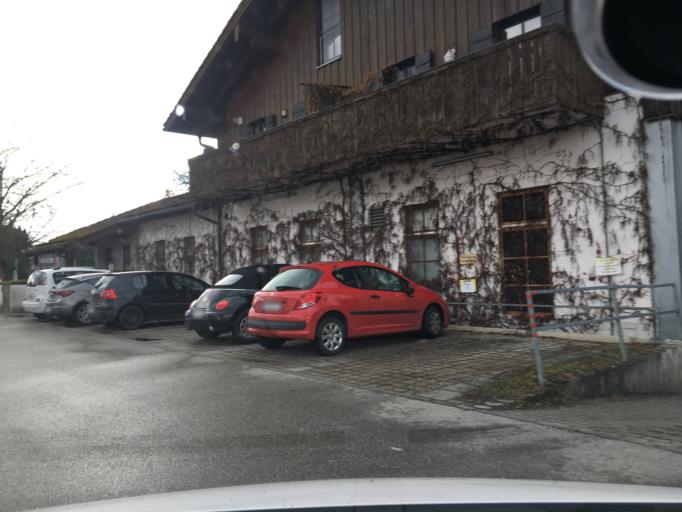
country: DE
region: Bavaria
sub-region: Upper Bavaria
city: Riedering
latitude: 47.8374
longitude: 12.2096
